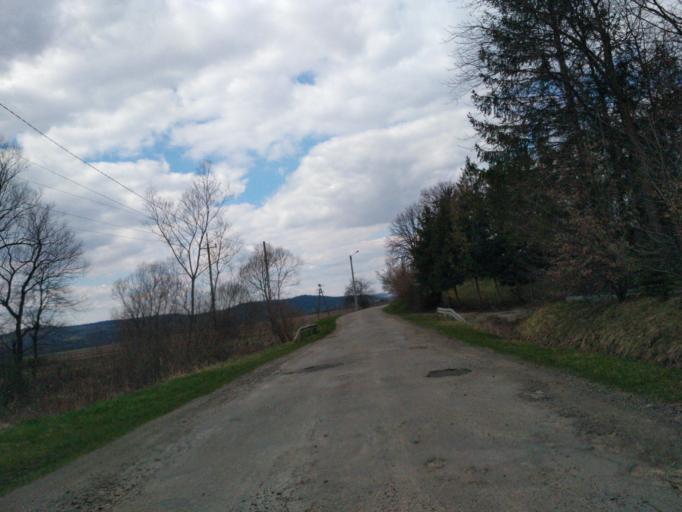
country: PL
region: Subcarpathian Voivodeship
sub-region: Powiat sanocki
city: Tyrawa Woloska
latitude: 49.6649
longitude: 22.2909
